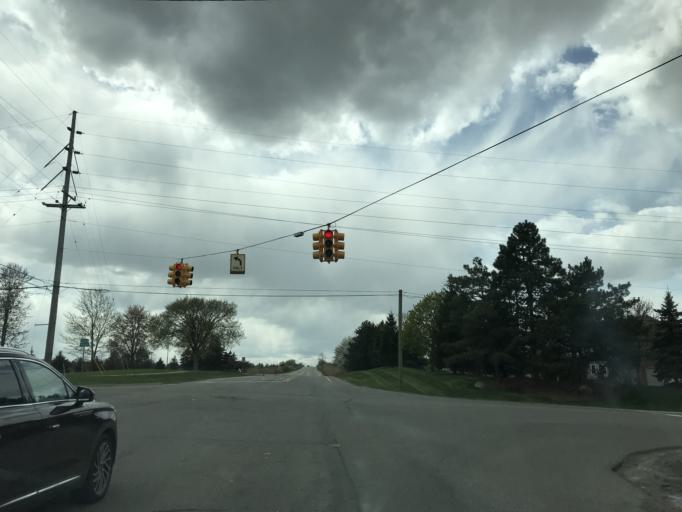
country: US
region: Michigan
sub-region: Wayne County
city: Plymouth
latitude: 42.3760
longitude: -83.5287
